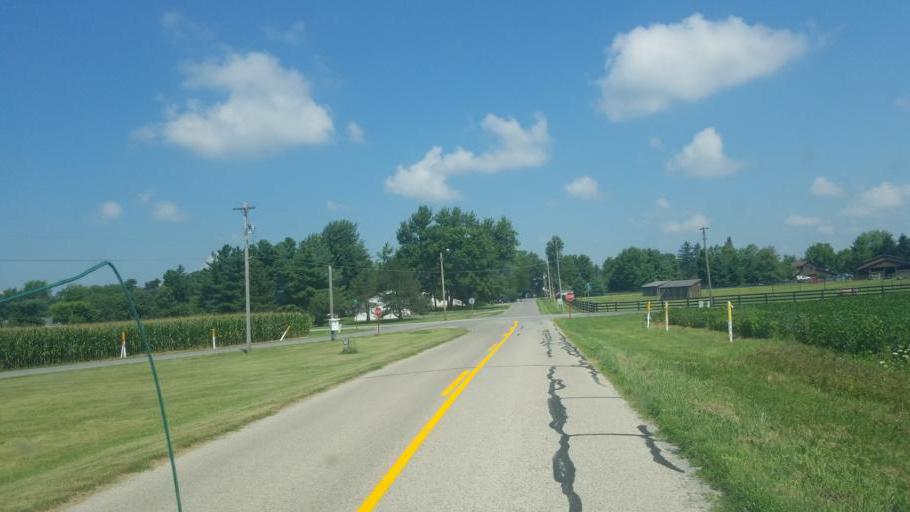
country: US
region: Ohio
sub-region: Hardin County
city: Ada
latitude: 40.7022
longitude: -83.9180
